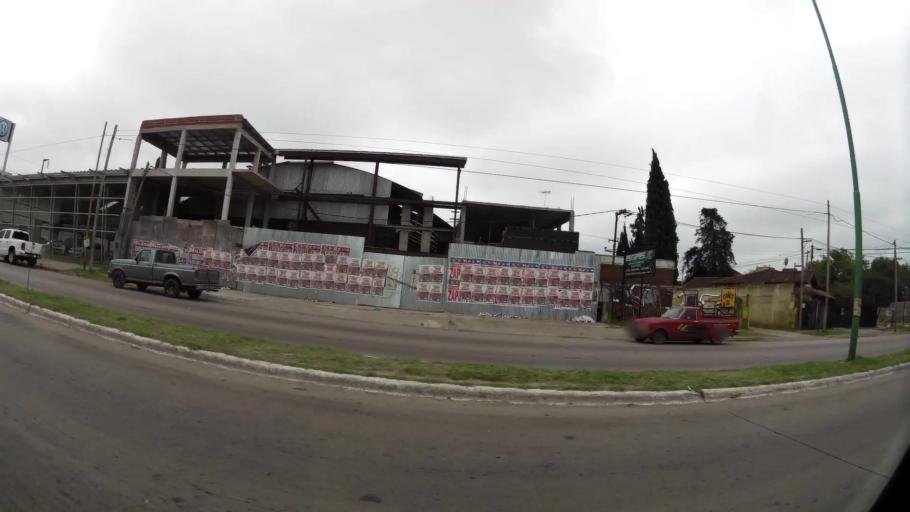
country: AR
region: Buenos Aires
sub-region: Partido de La Plata
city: La Plata
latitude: -34.9461
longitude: -57.9940
